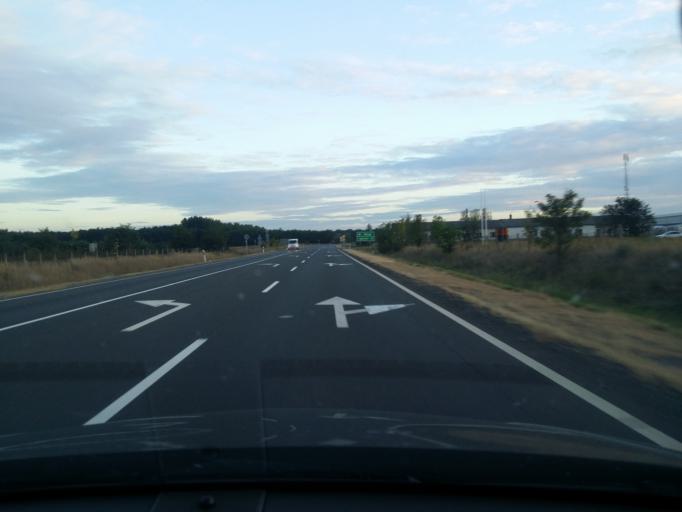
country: HU
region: Szabolcs-Szatmar-Bereg
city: Nyirpazony
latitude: 48.0132
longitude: 21.8438
